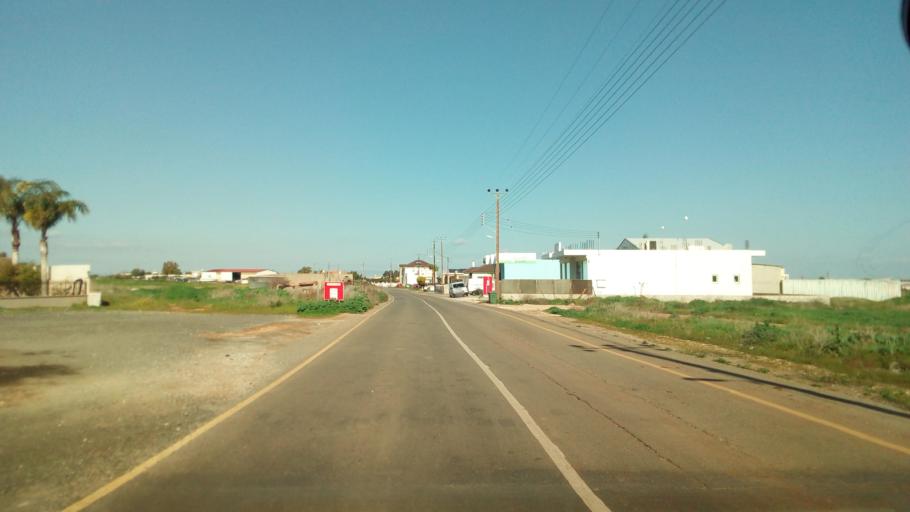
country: CY
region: Ammochostos
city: Liopetri
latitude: 34.9851
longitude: 33.8490
